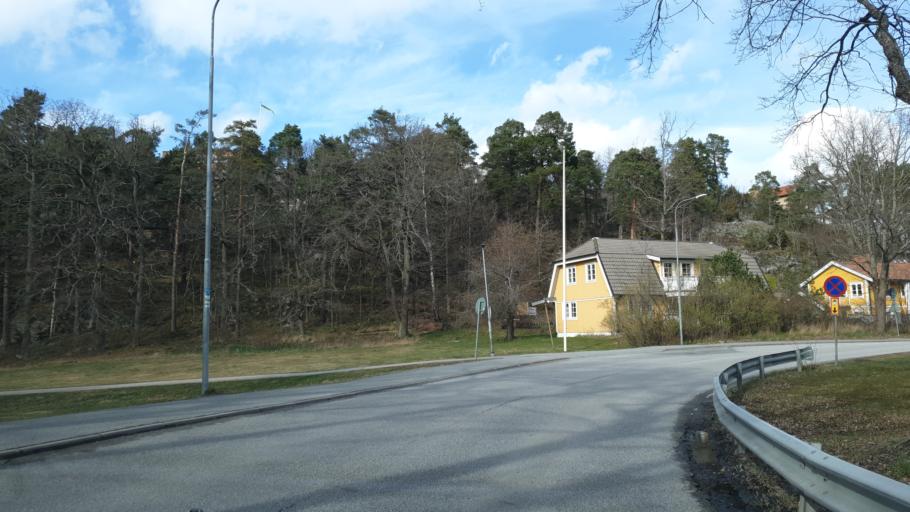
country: SE
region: Stockholm
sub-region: Nacka Kommun
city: Fisksatra
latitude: 59.2792
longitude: 18.2829
